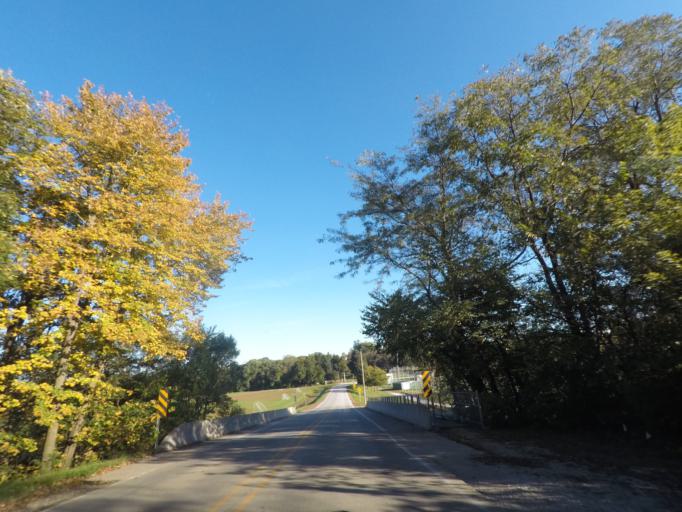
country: US
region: Iowa
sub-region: Story County
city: Nevada
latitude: 42.0173
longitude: -93.4629
